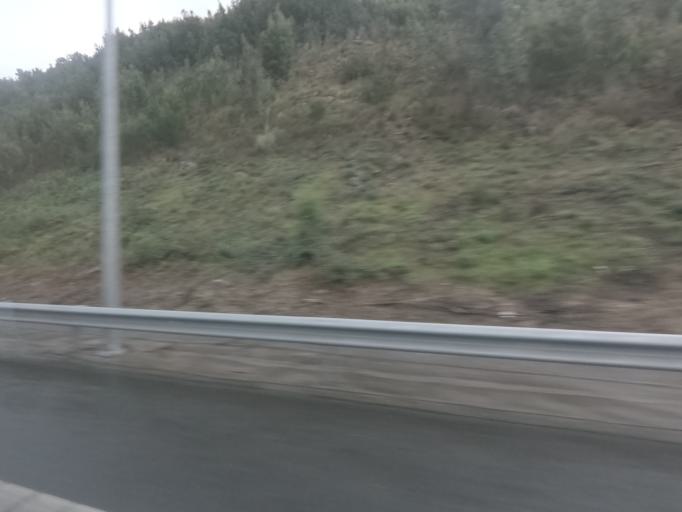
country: ES
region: Galicia
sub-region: Provincia de Pontevedra
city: Vigo
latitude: 42.2246
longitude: -8.6730
